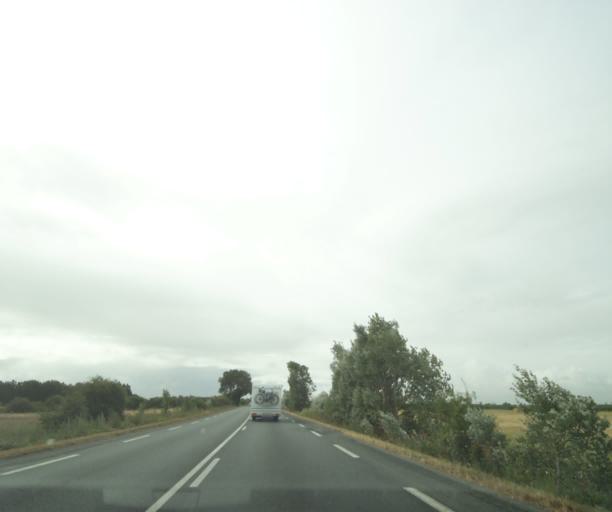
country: FR
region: Pays de la Loire
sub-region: Departement de la Vendee
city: Sainte-Gemme-la-Plaine
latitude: 46.4318
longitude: -1.0970
